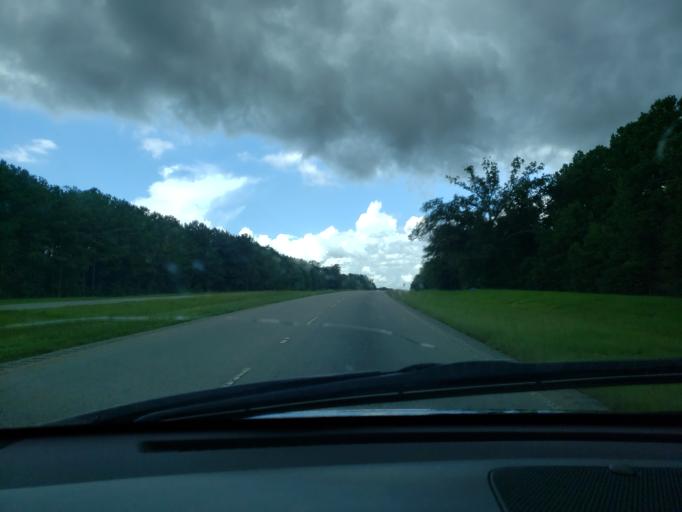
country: US
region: North Carolina
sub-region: Bladen County
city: Elizabethtown
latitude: 34.6116
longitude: -78.6395
